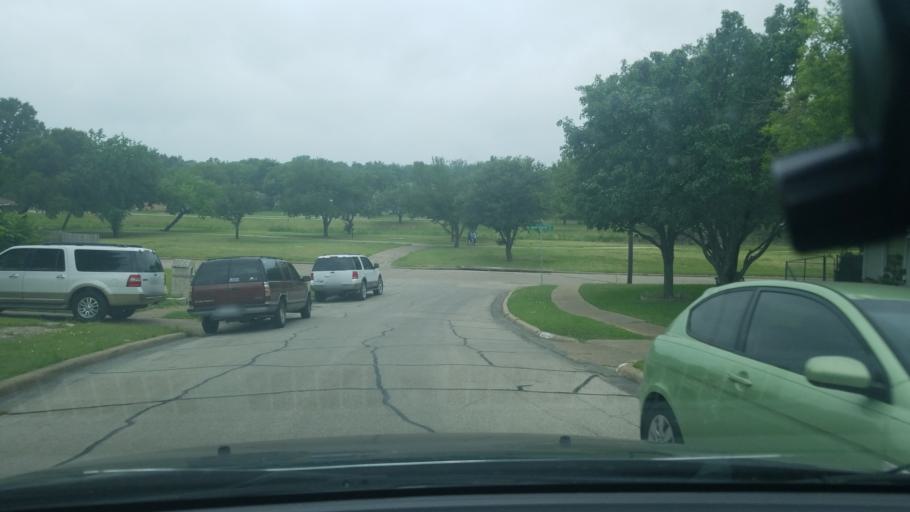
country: US
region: Texas
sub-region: Dallas County
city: Mesquite
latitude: 32.7863
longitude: -96.6324
